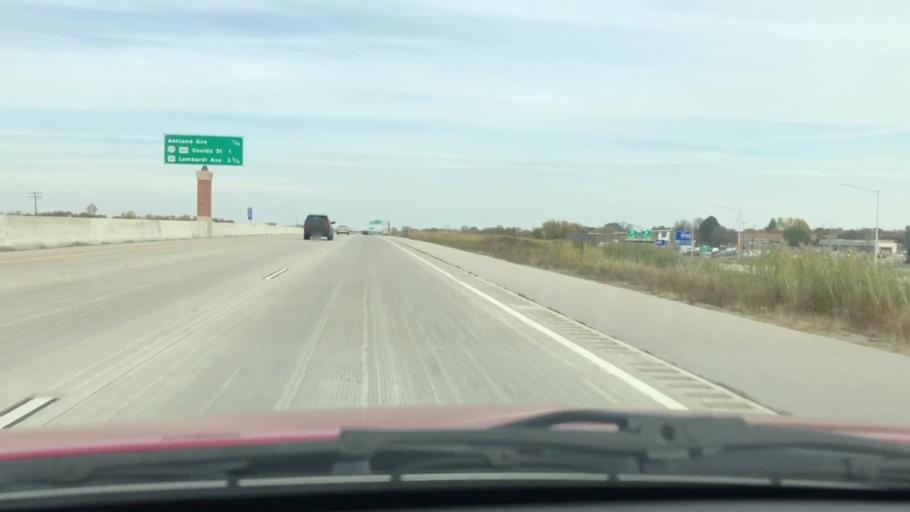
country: US
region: Wisconsin
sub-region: Brown County
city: De Pere
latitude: 44.4501
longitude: -88.0914
